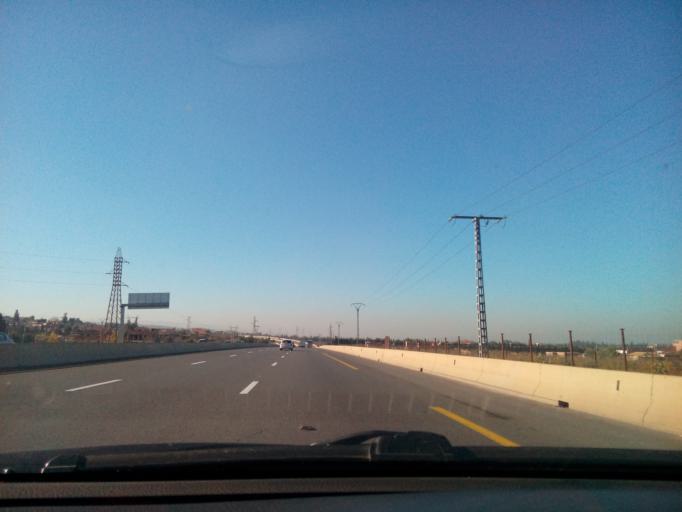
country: DZ
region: Chlef
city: Oued Sly
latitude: 36.0877
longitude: 1.1943
